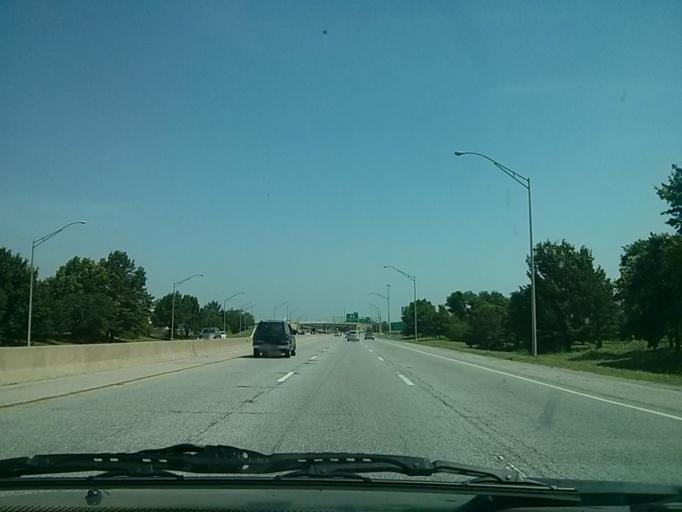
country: US
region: Oklahoma
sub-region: Tulsa County
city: Tulsa
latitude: 36.1237
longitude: -96.0085
